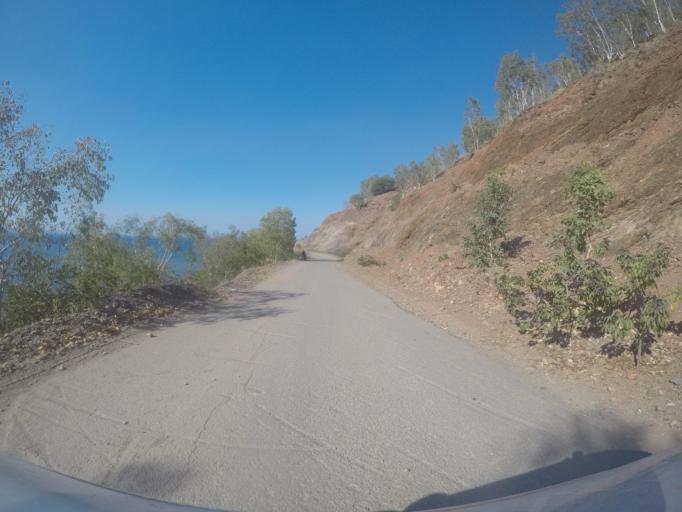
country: TL
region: Dili
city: Dili
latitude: -8.5277
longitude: 125.6272
